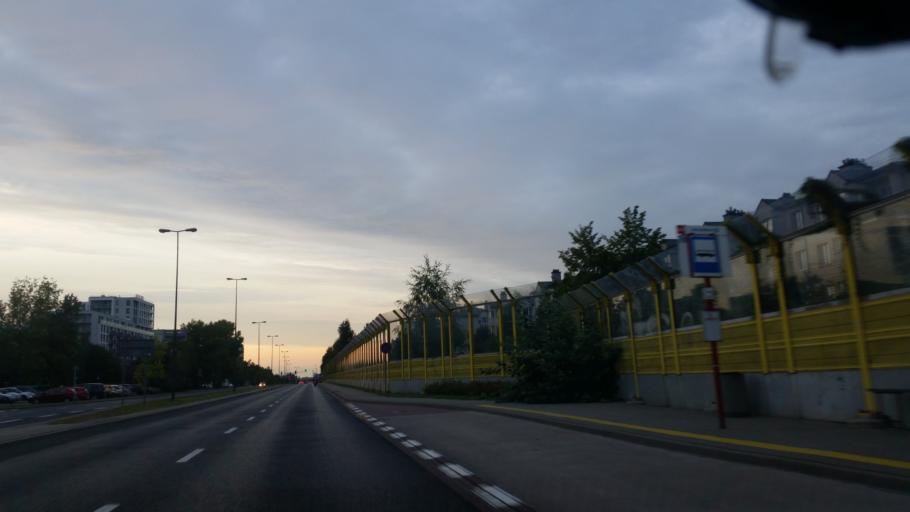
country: PL
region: Masovian Voivodeship
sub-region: Warszawa
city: Kabaty
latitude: 52.1397
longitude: 21.0688
